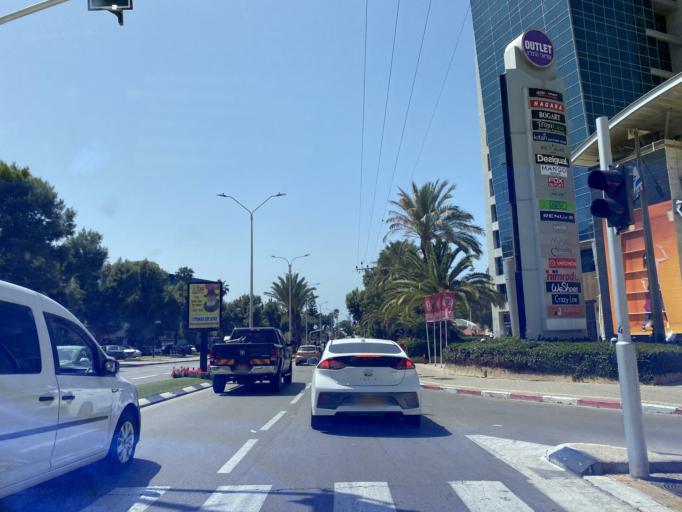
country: IL
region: Tel Aviv
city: Herzliya Pituah
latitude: 32.1661
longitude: 34.8105
